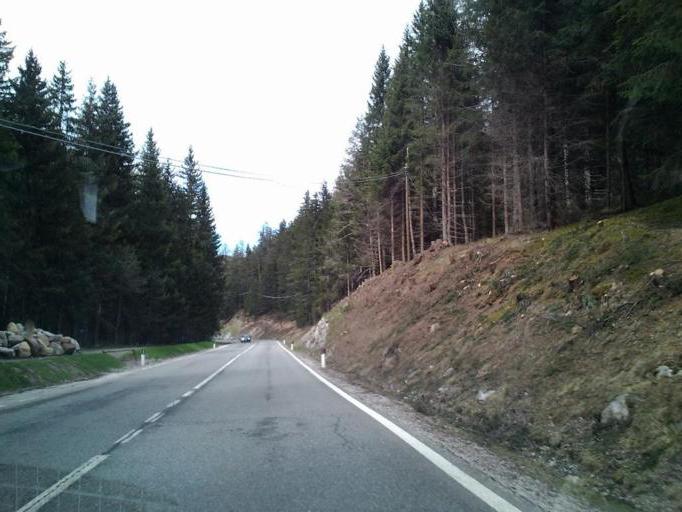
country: IT
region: Trentino-Alto Adige
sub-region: Bolzano
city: Dobbiaco
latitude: 46.7094
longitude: 12.2236
